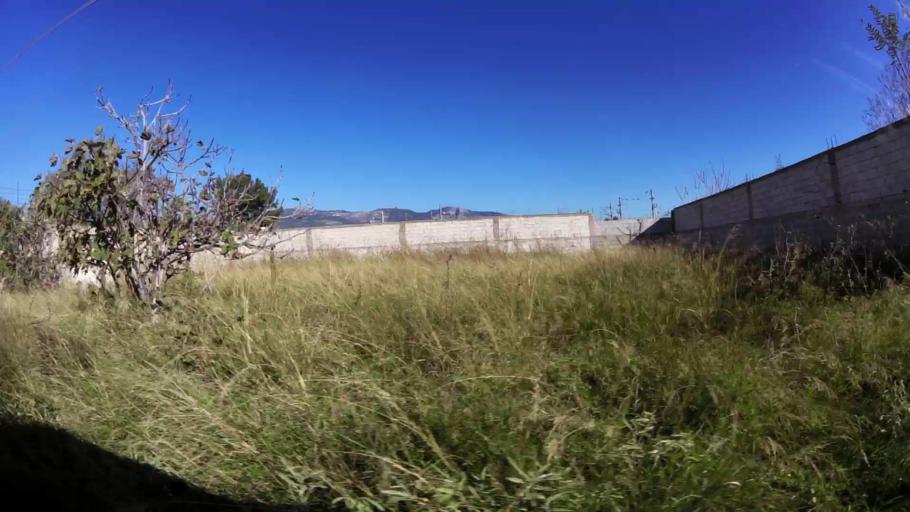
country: GR
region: Attica
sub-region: Nomarchia Anatolikis Attikis
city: Acharnes
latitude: 38.0798
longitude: 23.7493
